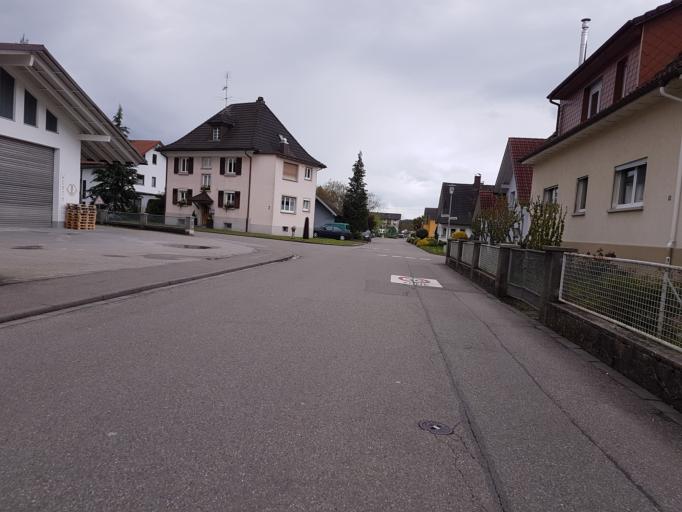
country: DE
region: Baden-Wuerttemberg
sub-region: Freiburg Region
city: Wutoschingen
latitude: 47.6610
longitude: 8.3643
